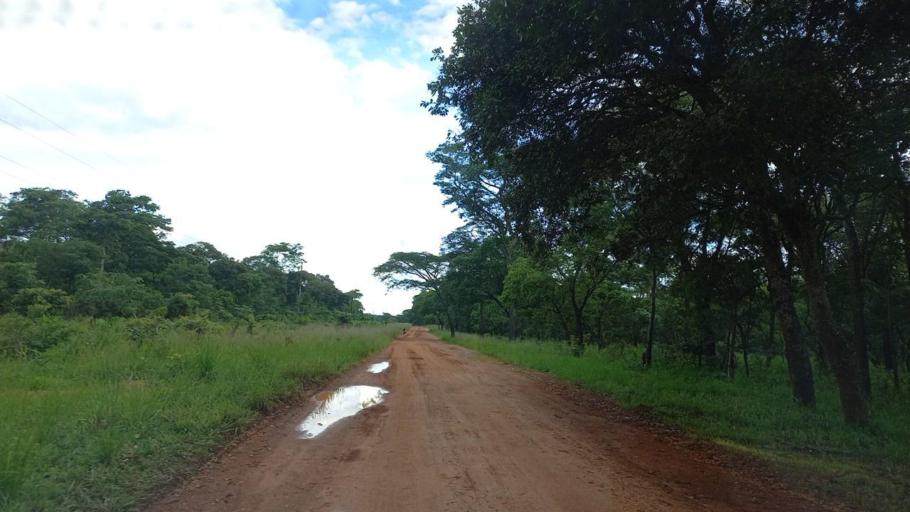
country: ZM
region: North-Western
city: Mwinilunga
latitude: -11.7949
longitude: 24.3716
